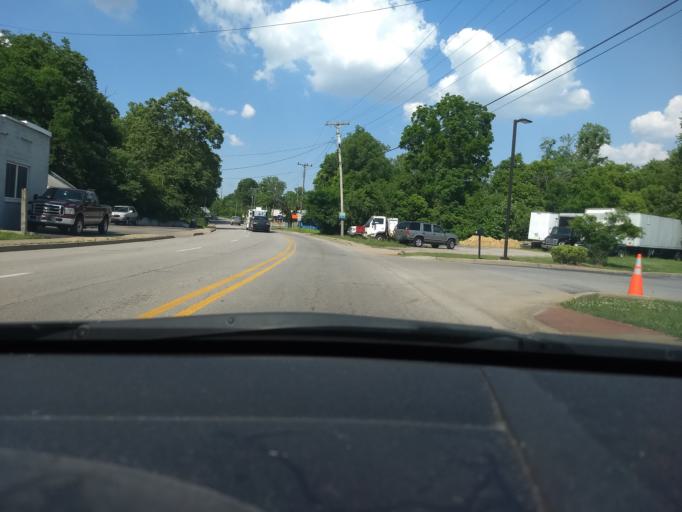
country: US
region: Indiana
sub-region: Floyd County
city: New Albany
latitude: 38.2744
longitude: -85.8376
